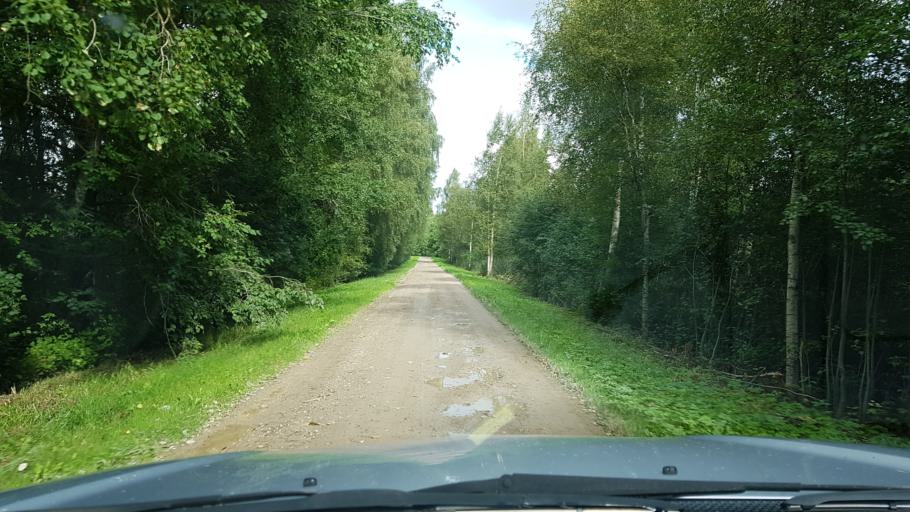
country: EE
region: Harju
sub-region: Raasiku vald
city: Arukula
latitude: 59.3016
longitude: 25.0704
